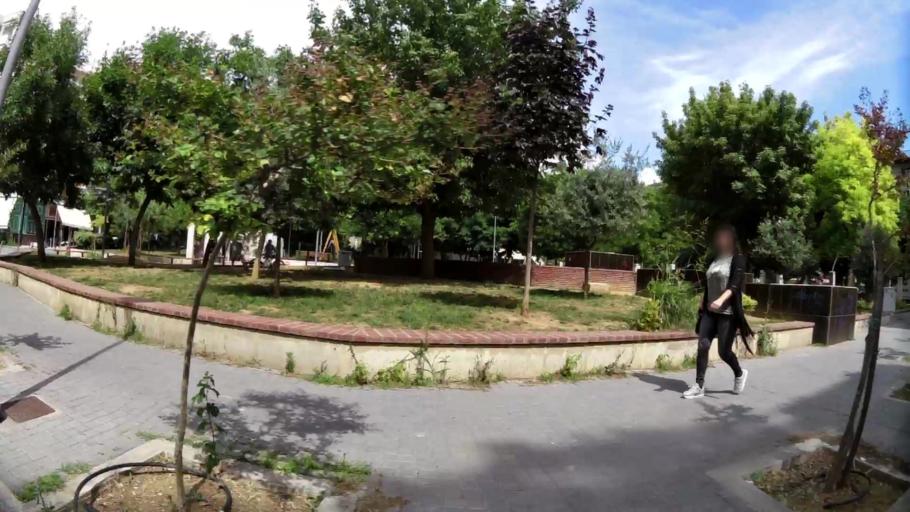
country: GR
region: Central Macedonia
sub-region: Nomos Thessalonikis
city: Triandria
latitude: 40.6029
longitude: 22.9614
